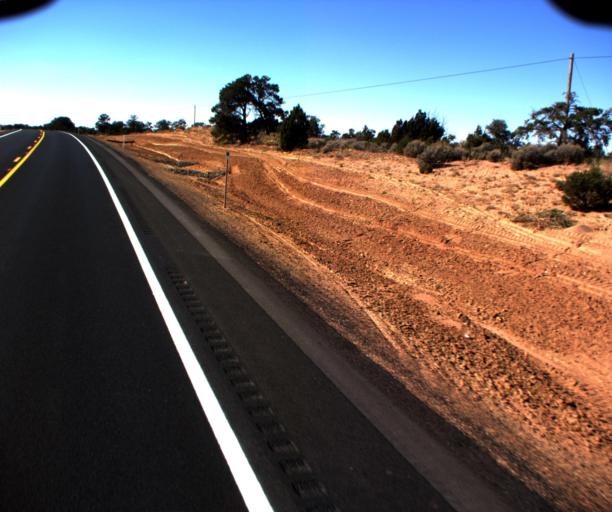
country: US
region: Arizona
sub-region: Apache County
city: Ganado
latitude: 35.7195
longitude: -109.3673
